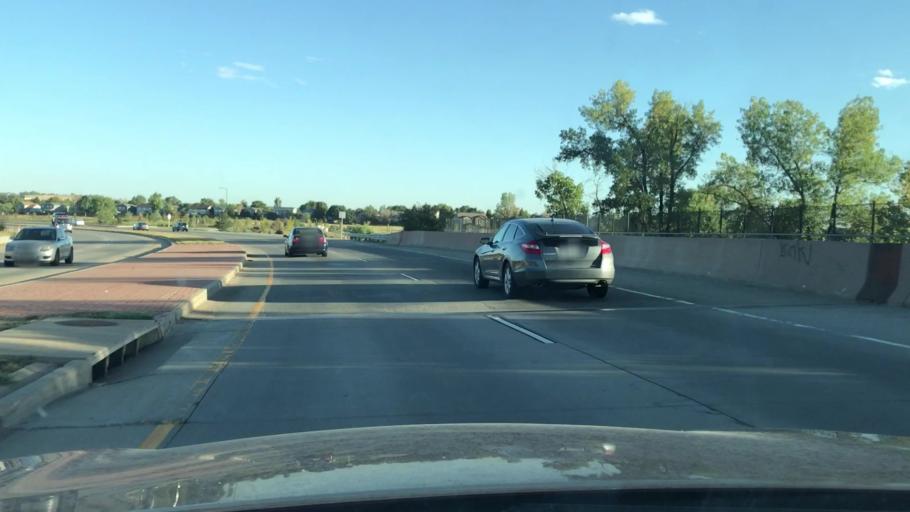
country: US
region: Colorado
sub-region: Boulder County
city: Lafayette
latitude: 39.9801
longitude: -105.0981
